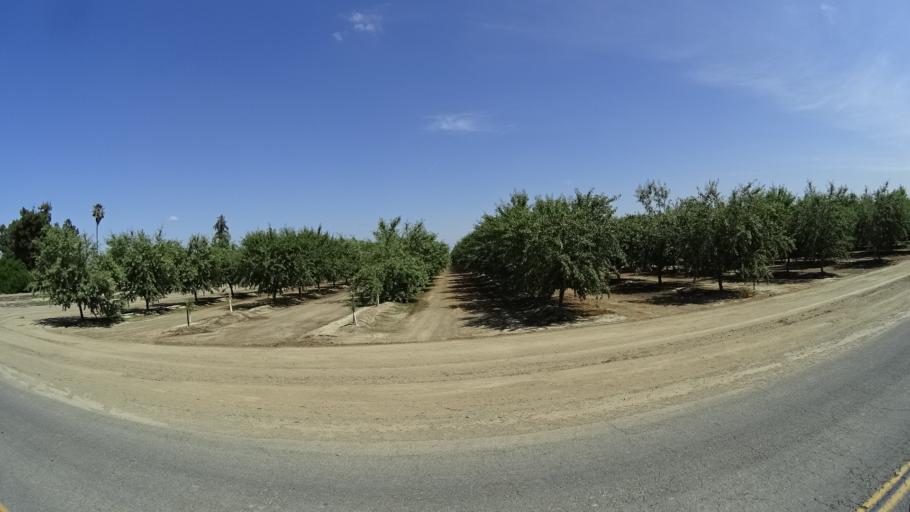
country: US
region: California
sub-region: Kings County
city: Home Garden
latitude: 36.2695
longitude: -119.5641
